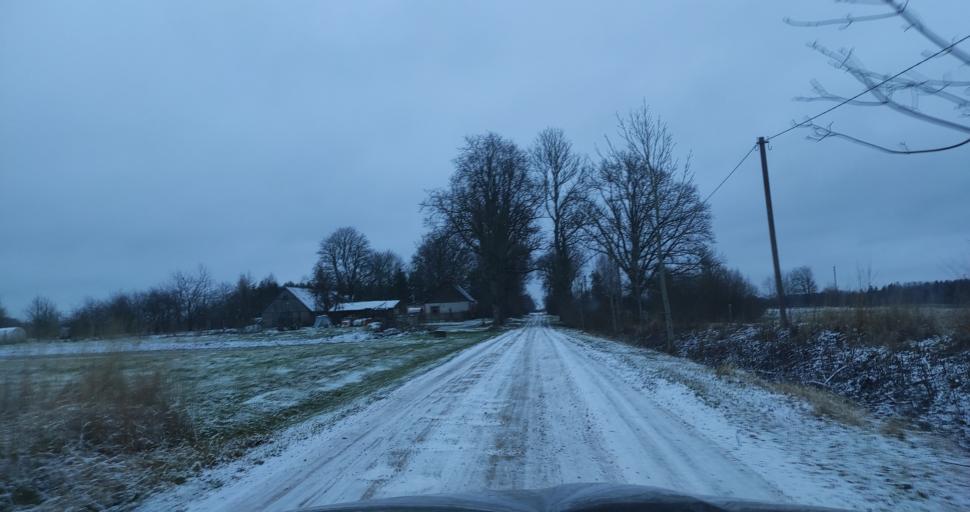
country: LV
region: Kuldigas Rajons
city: Kuldiga
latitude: 56.9739
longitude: 22.0568
